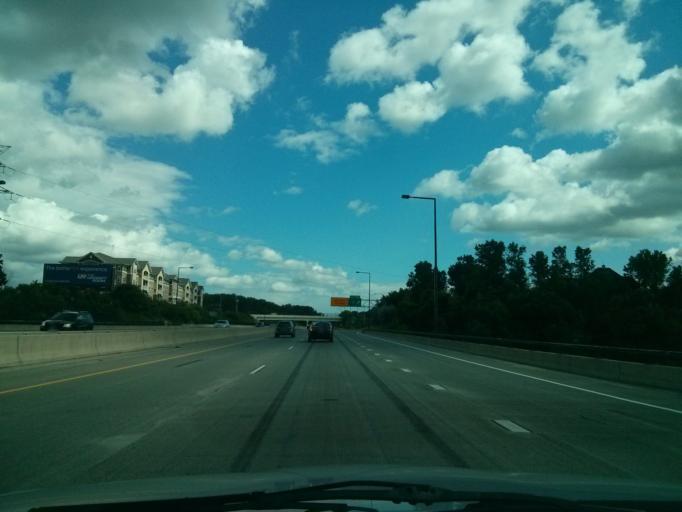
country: US
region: Minnesota
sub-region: Dakota County
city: Mendota Heights
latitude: 44.9043
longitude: -93.1392
